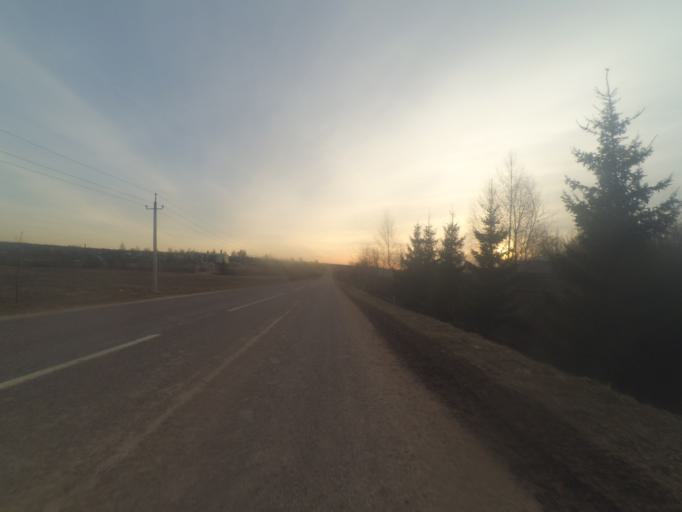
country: RU
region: Moskovskaya
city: Karinskoye
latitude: 55.7733
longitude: 36.5903
